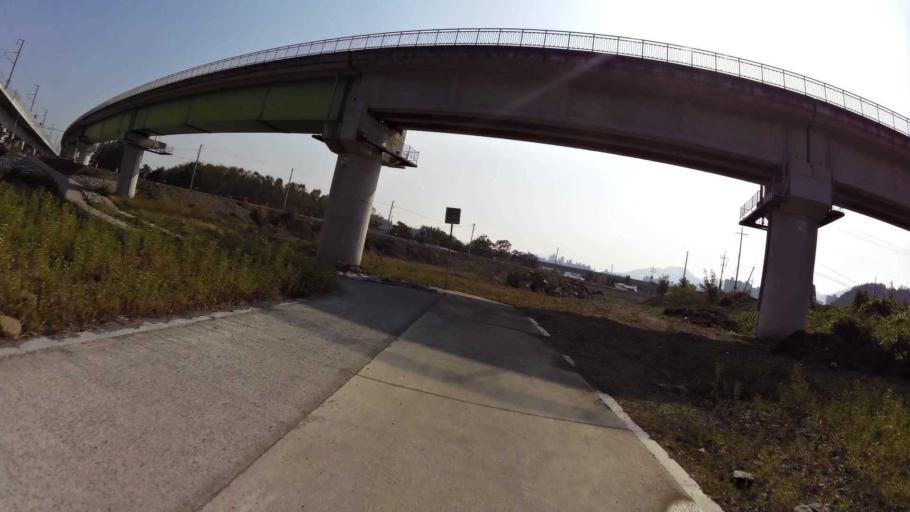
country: KR
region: Gyeongsangbuk-do
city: Gyeongsan-si
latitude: 35.8542
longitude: 128.7082
